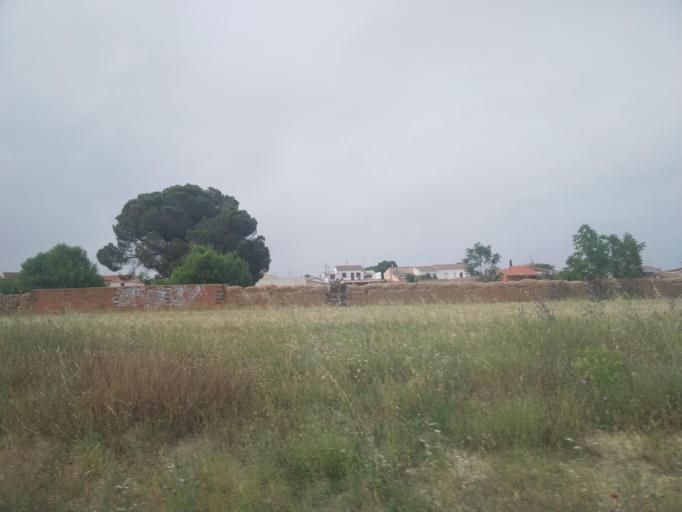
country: ES
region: Castille-La Mancha
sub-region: Province of Toledo
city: Casasbuenas
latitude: 39.7594
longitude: -4.1279
